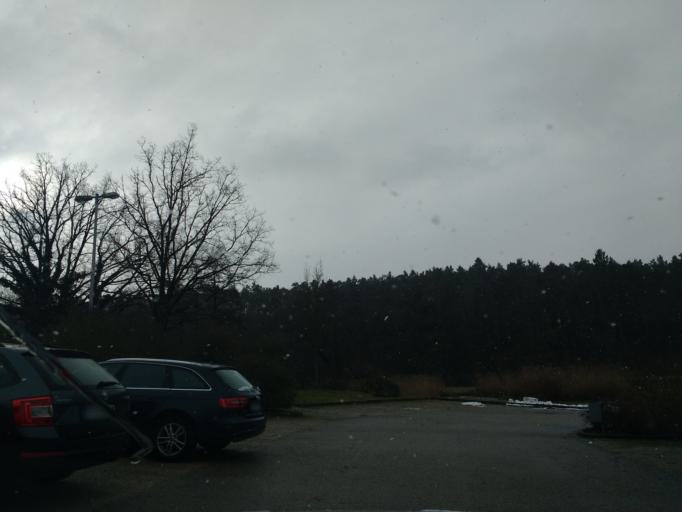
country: DE
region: Bavaria
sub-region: Regierungsbezirk Mittelfranken
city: Herzogenaurach
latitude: 49.5727
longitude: 10.8664
